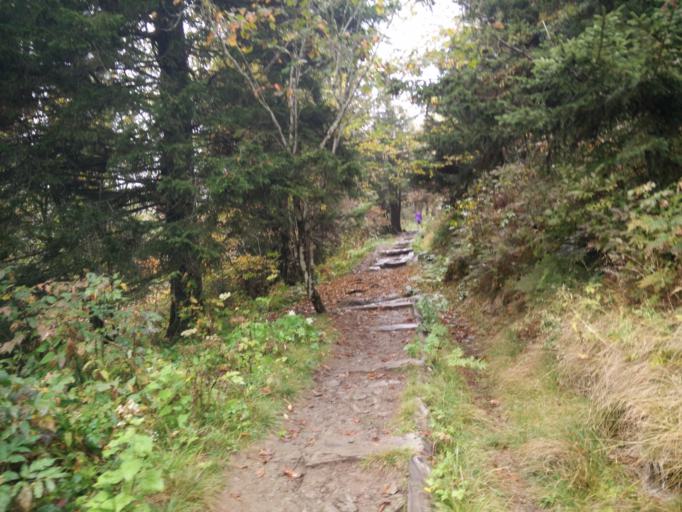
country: US
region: North Carolina
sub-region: Swain County
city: Bryson City
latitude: 35.5521
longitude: -83.4925
